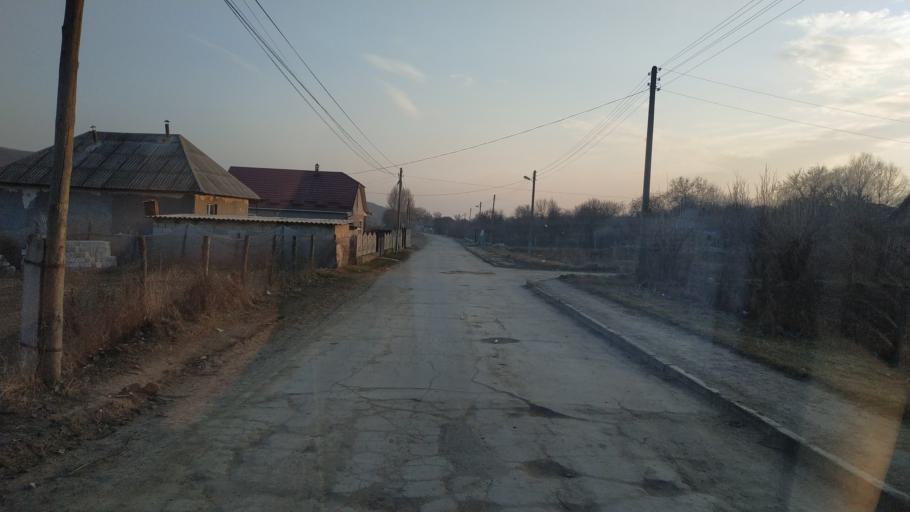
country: MD
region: Hincesti
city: Dancu
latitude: 46.7104
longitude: 28.3455
